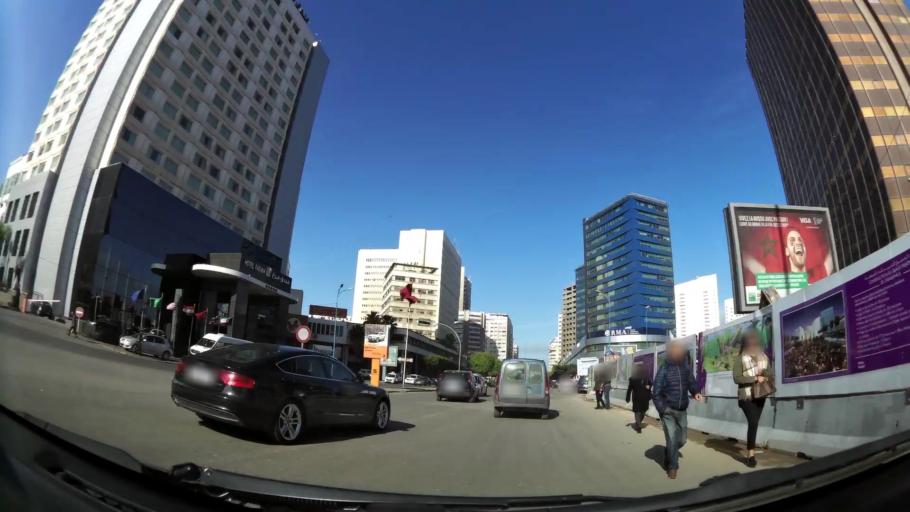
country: MA
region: Grand Casablanca
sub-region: Casablanca
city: Casablanca
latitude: 33.5969
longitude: -7.6098
